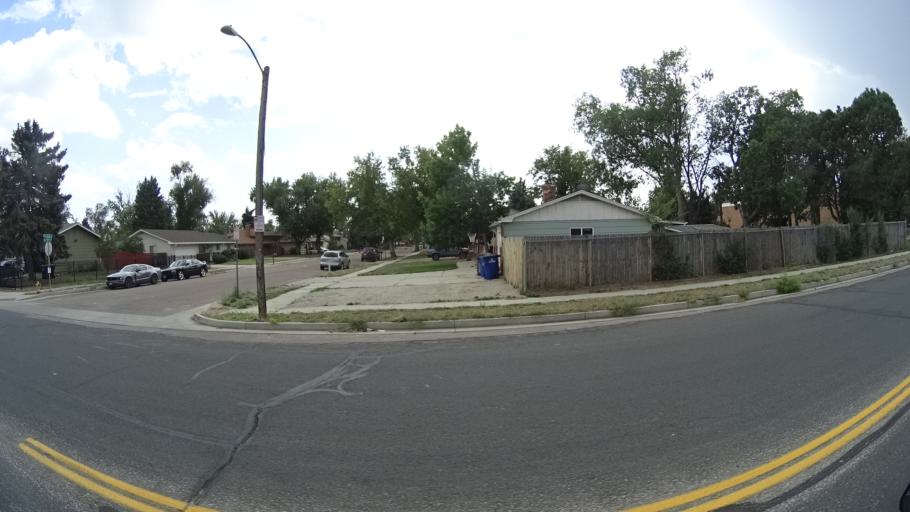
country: US
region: Colorado
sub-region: El Paso County
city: Cimarron Hills
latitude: 38.8508
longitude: -104.7491
